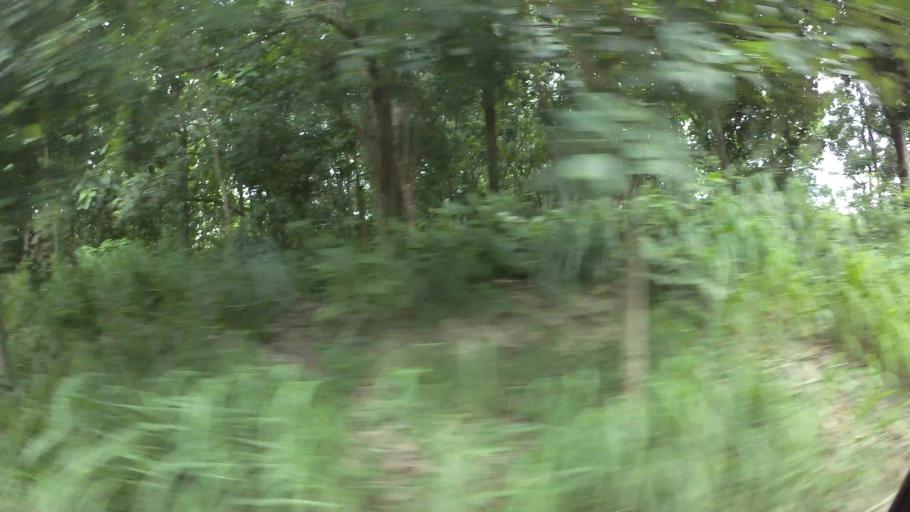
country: TH
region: Chon Buri
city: Si Racha
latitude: 13.1616
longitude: 100.9786
